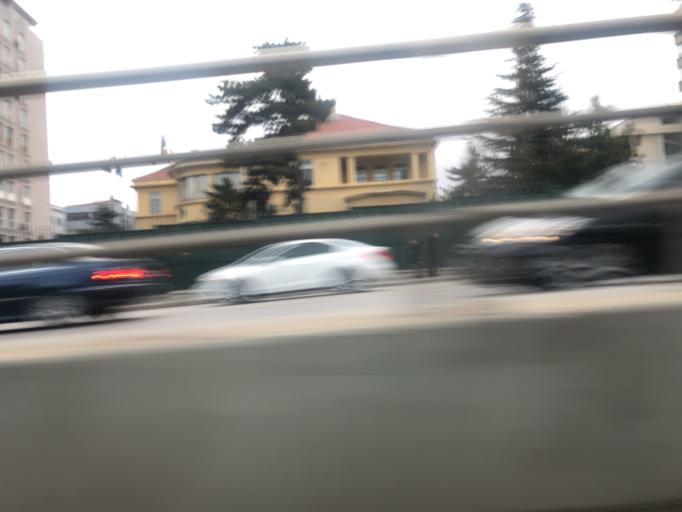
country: TR
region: Ankara
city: Ankara
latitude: 39.9154
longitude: 32.8541
